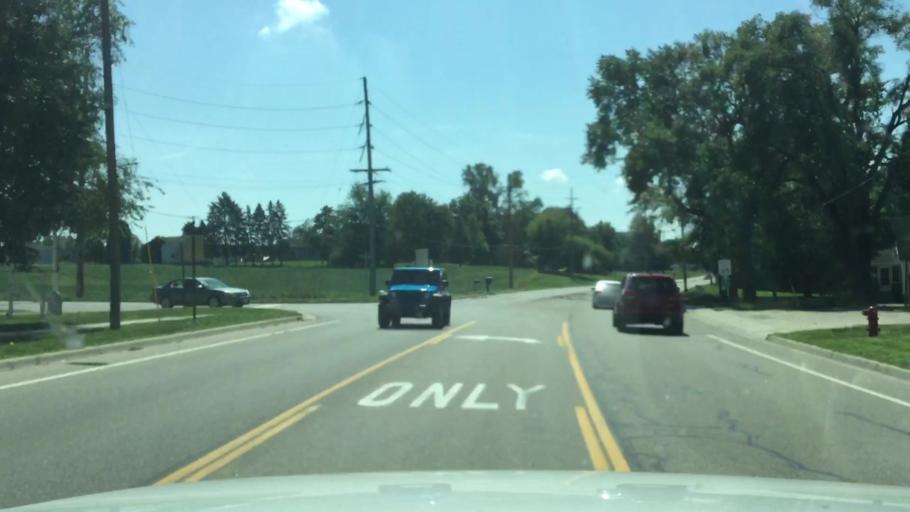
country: US
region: Michigan
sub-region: Lenawee County
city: Clinton
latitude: 42.0651
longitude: -83.9671
